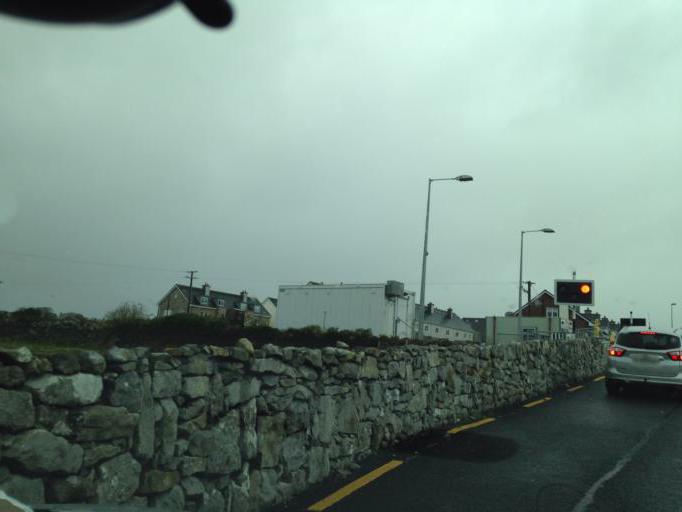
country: IE
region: Connaught
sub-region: County Galway
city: Oranmore
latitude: 53.2728
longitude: -8.9735
